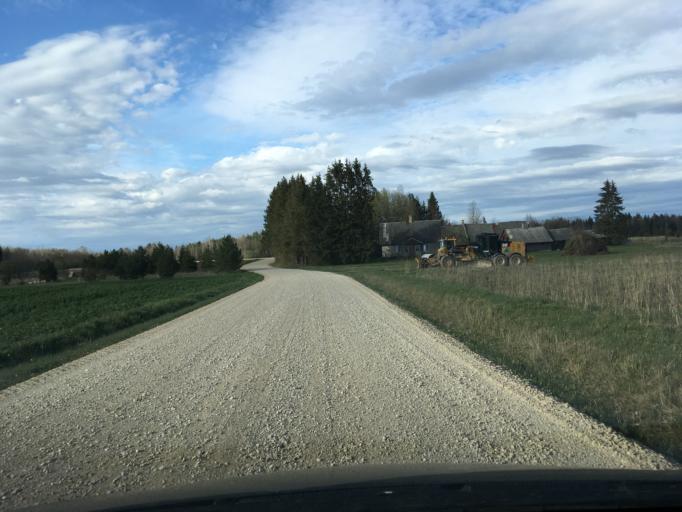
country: EE
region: Raplamaa
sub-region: Maerjamaa vald
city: Marjamaa
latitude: 58.9797
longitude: 24.3612
